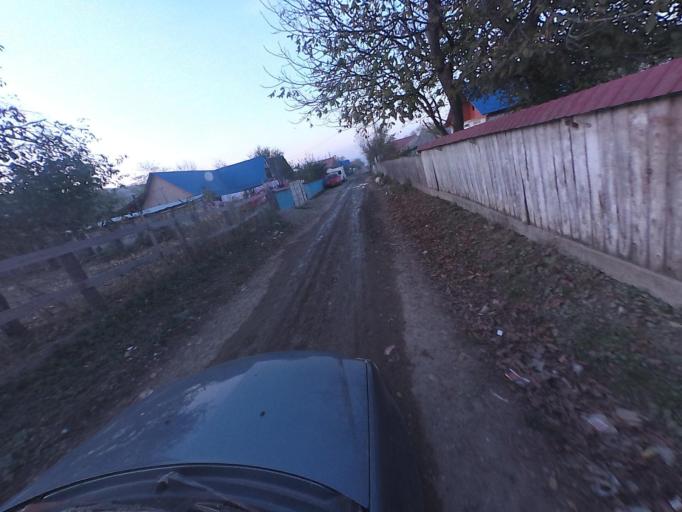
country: RO
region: Vaslui
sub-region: Comuna Garceni
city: Garceni
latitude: 46.7889
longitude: 27.2437
